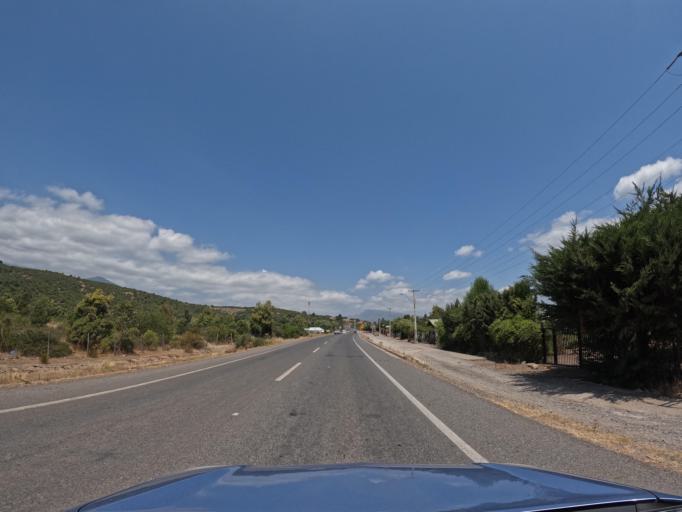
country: CL
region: Maule
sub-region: Provincia de Curico
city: Molina
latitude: -35.1764
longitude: -71.1220
